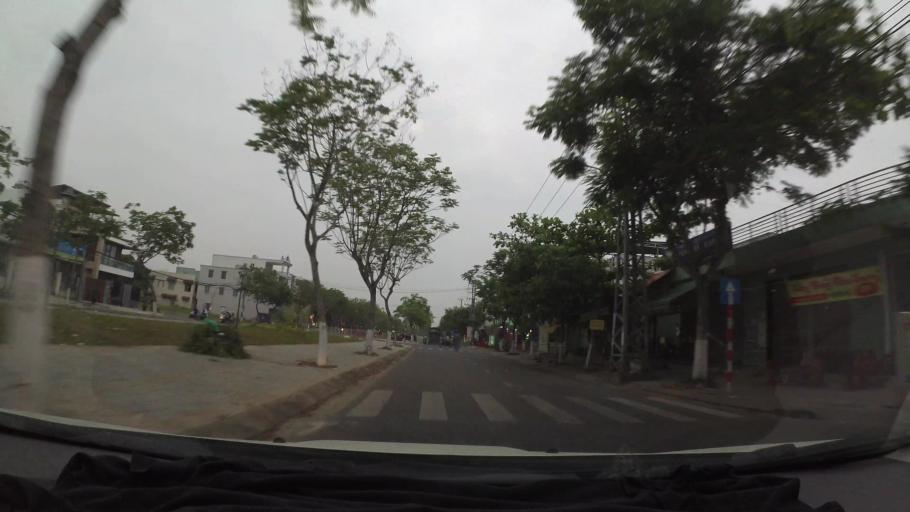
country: VN
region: Da Nang
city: Thanh Khe
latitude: 16.0540
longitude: 108.1773
